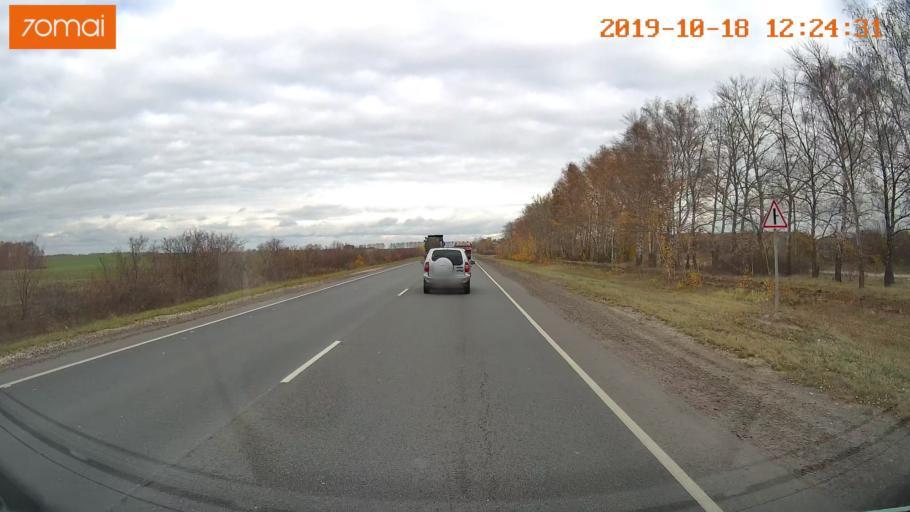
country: RU
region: Rjazan
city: Rybnoye
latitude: 54.5398
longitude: 39.5137
